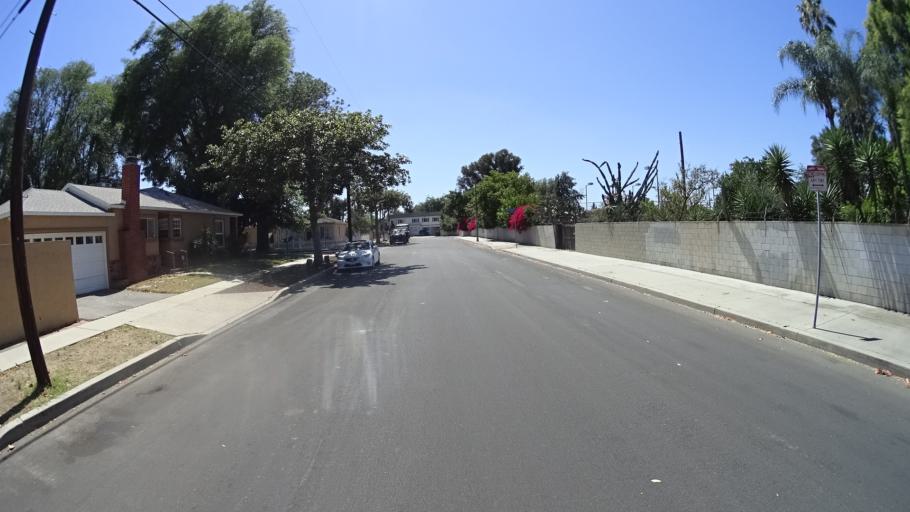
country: US
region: California
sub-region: Los Angeles County
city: Van Nuys
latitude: 34.1929
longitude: -118.4955
